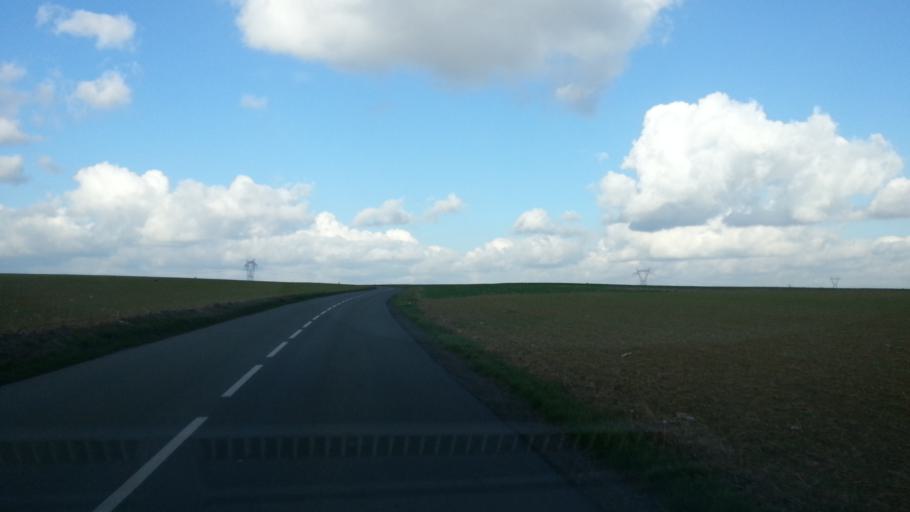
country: FR
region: Picardie
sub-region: Departement de l'Oise
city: Villers-sous-Saint-Leu
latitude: 49.2251
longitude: 2.4144
